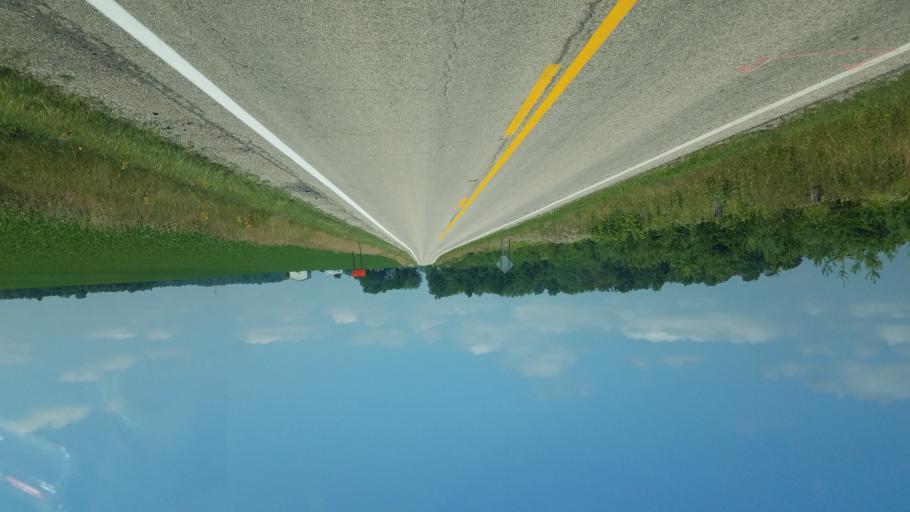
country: US
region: Ohio
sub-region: Crawford County
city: Bucyrus
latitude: 40.8431
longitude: -82.8556
